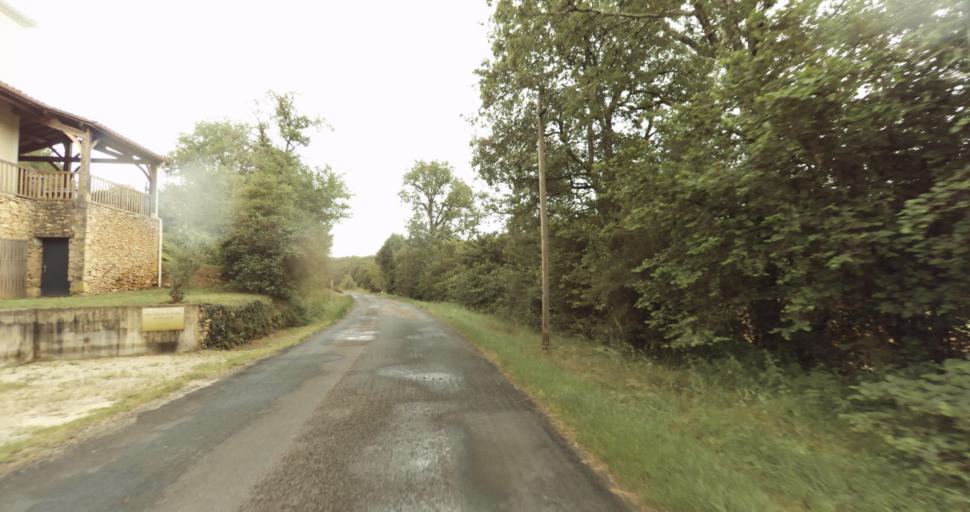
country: FR
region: Aquitaine
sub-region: Departement de la Dordogne
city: Belves
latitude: 44.7558
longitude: 0.9239
